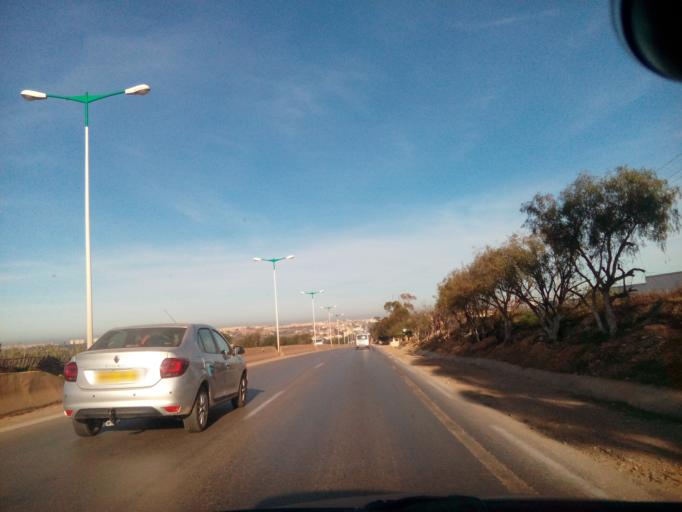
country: DZ
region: Mostaganem
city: Mostaganem
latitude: 35.8935
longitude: 0.1284
